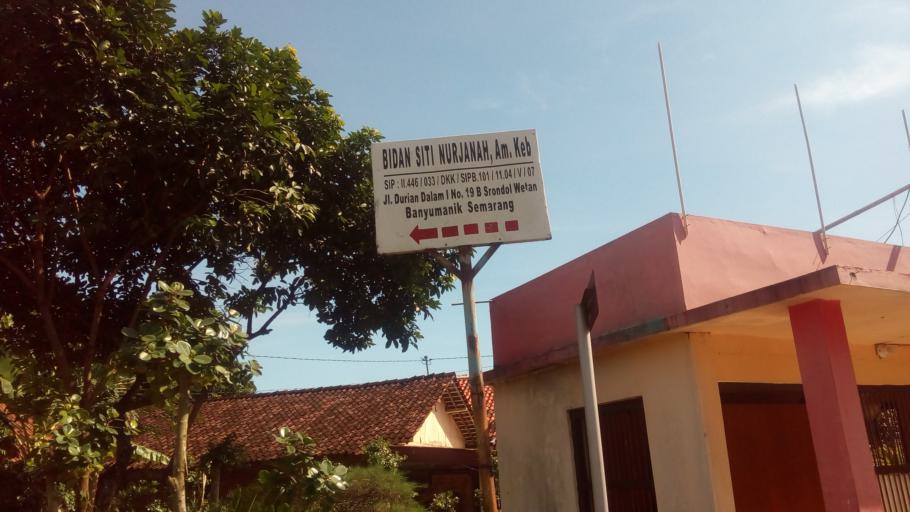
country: ID
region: Central Java
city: Semarang
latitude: -7.0606
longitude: 110.4212
